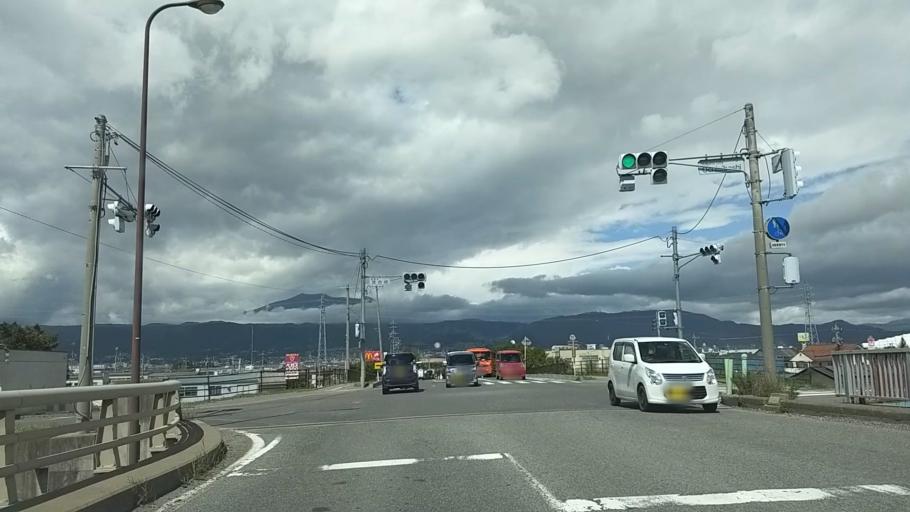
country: JP
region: Nagano
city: Nagano-shi
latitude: 36.6249
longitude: 138.2378
